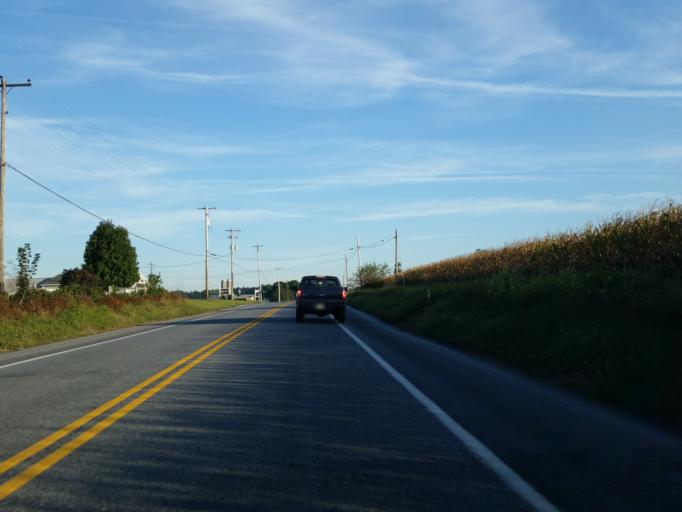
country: US
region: Pennsylvania
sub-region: Lancaster County
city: Quarryville
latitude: 39.8441
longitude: -76.2190
